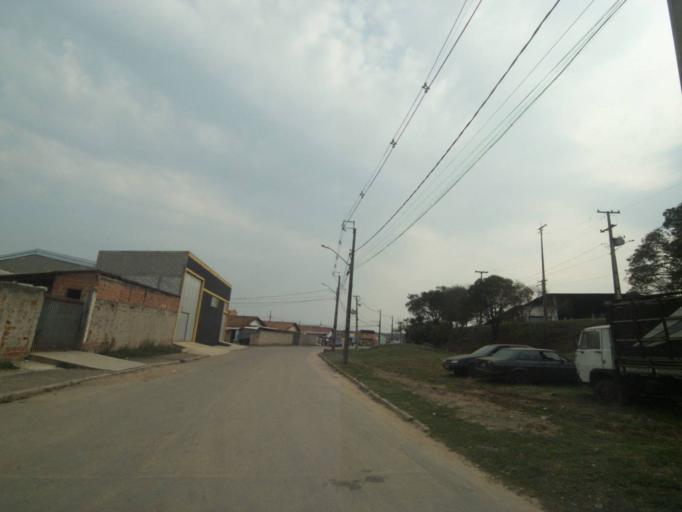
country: BR
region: Parana
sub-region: Sao Jose Dos Pinhais
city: Sao Jose dos Pinhais
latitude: -25.5322
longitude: -49.2303
